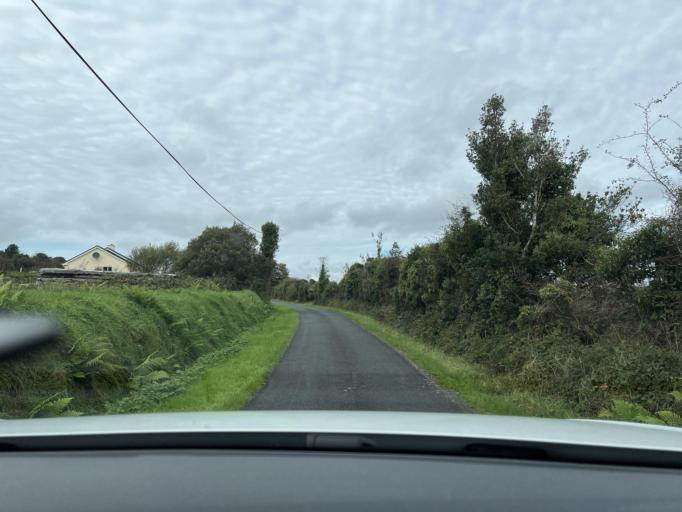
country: IE
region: Connaught
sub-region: Roscommon
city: Boyle
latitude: 54.0005
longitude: -8.2798
